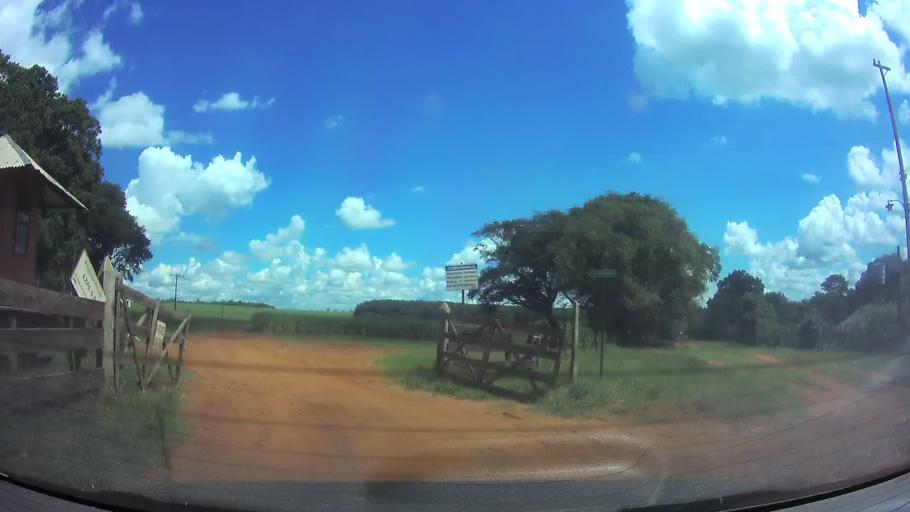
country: PY
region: Paraguari
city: La Colmena
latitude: -25.9506
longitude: -56.7827
